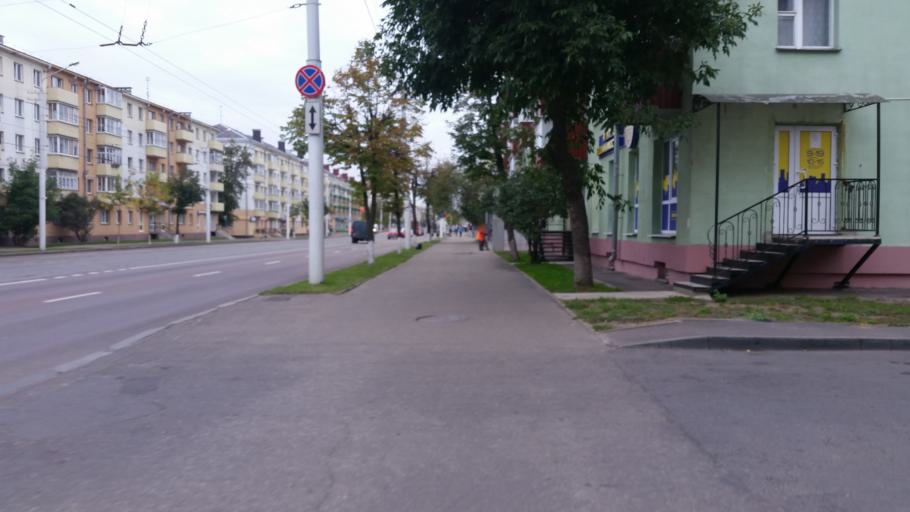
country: BY
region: Vitebsk
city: Vitebsk
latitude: 55.1760
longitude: 30.2007
